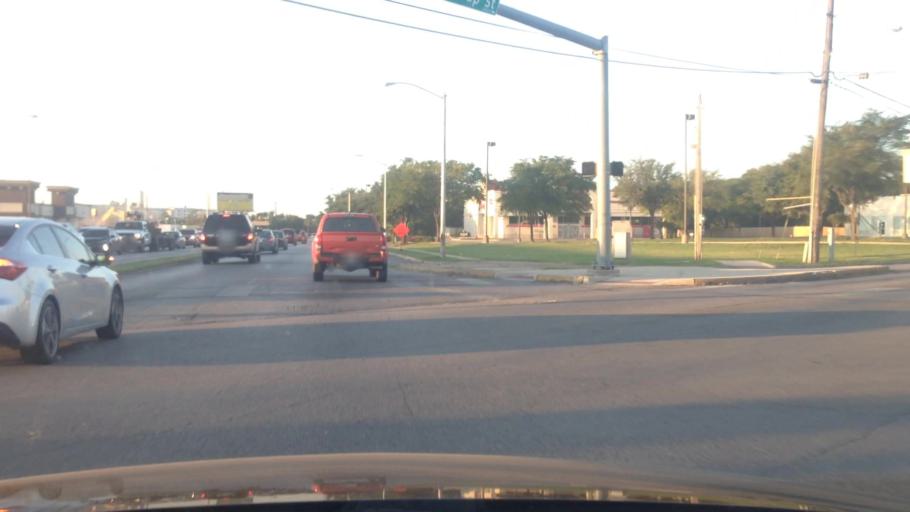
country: US
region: Texas
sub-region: Tarrant County
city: Haltom City
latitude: 32.7810
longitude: -97.2908
